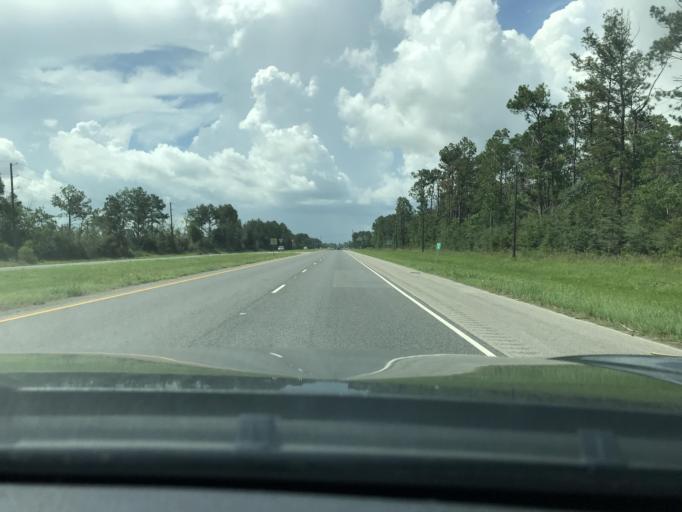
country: US
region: Louisiana
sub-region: Calcasieu Parish
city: Moss Bluff
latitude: 30.3405
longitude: -93.2004
